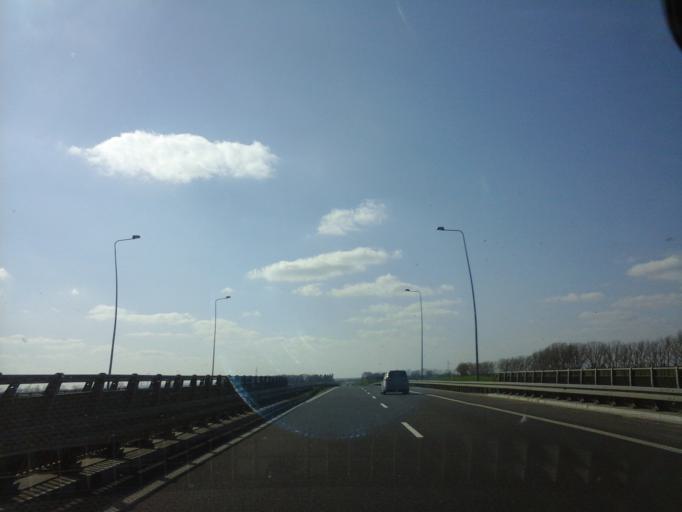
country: PL
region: West Pomeranian Voivodeship
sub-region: Powiat stargardzki
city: Stargard Szczecinski
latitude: 53.3075
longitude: 15.0216
